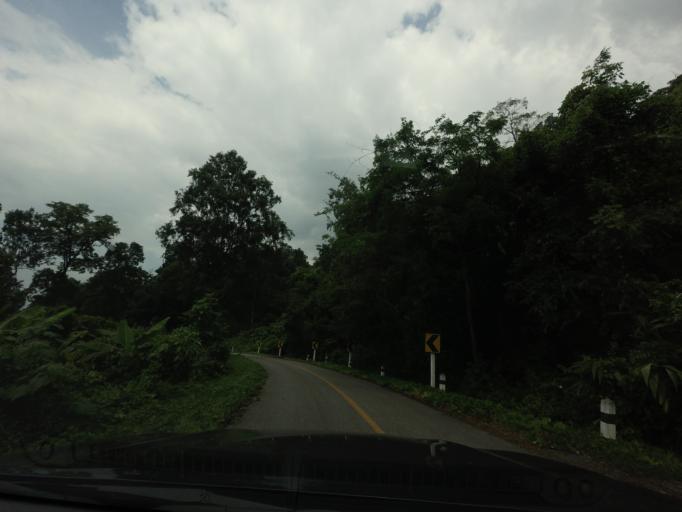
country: TH
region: Uttaradit
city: Nam Pat
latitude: 17.7363
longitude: 100.9488
